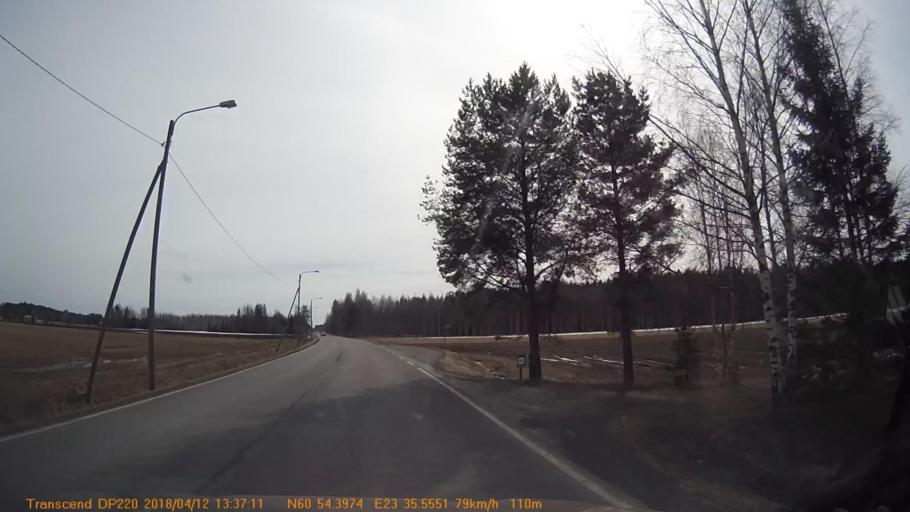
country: FI
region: Haeme
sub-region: Forssa
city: Forssa
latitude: 60.9064
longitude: 23.5926
